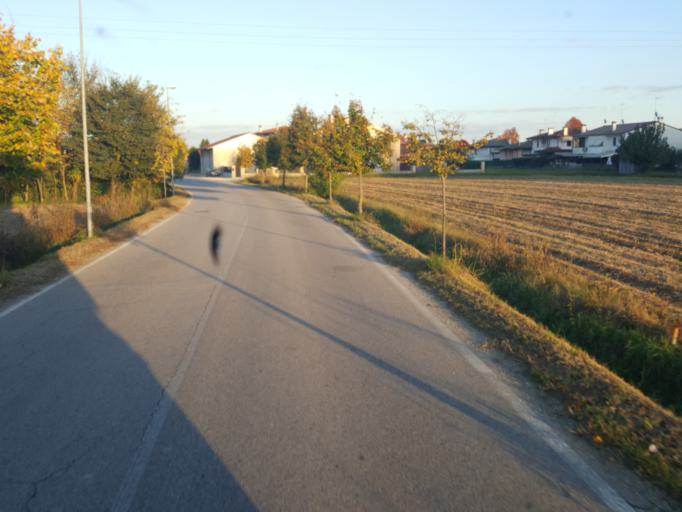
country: IT
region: Veneto
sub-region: Provincia di Treviso
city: Sant'Andrea
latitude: 45.6559
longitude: 11.9044
